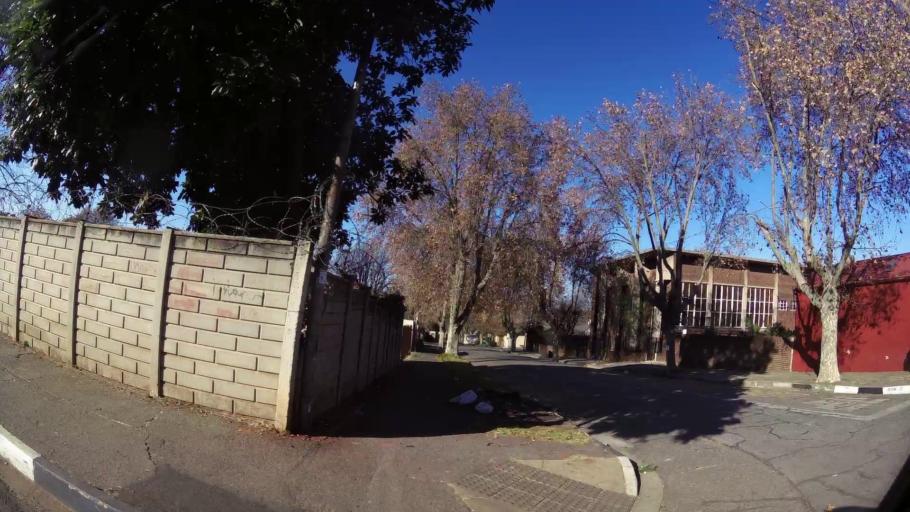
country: ZA
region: Gauteng
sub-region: City of Johannesburg Metropolitan Municipality
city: Johannesburg
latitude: -26.2031
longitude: 28.0751
